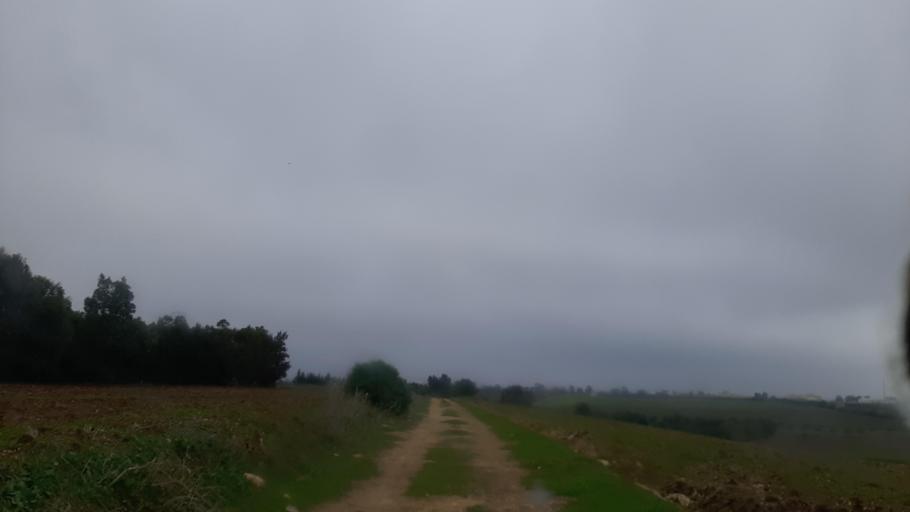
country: TN
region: Nabul
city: Qulaybiyah
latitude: 36.8284
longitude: 11.0342
